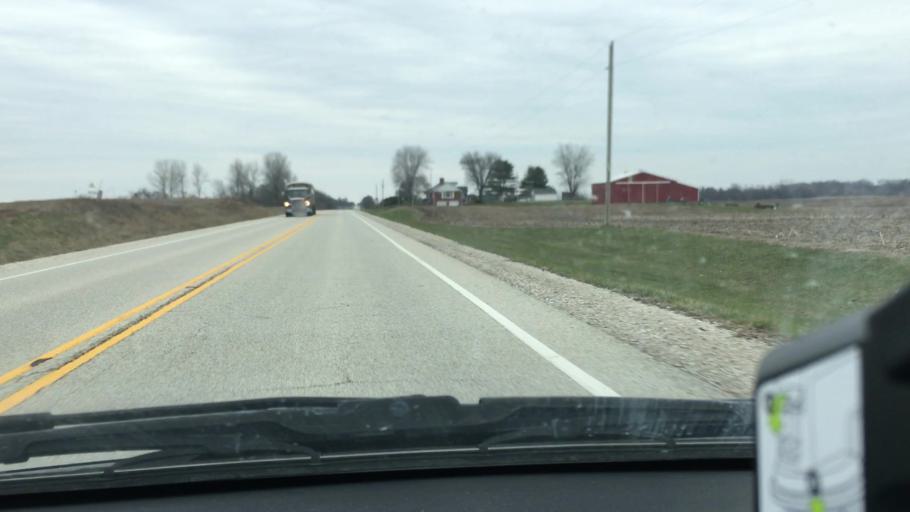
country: US
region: Indiana
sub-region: Daviess County
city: Odon
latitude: 38.9419
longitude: -87.0168
